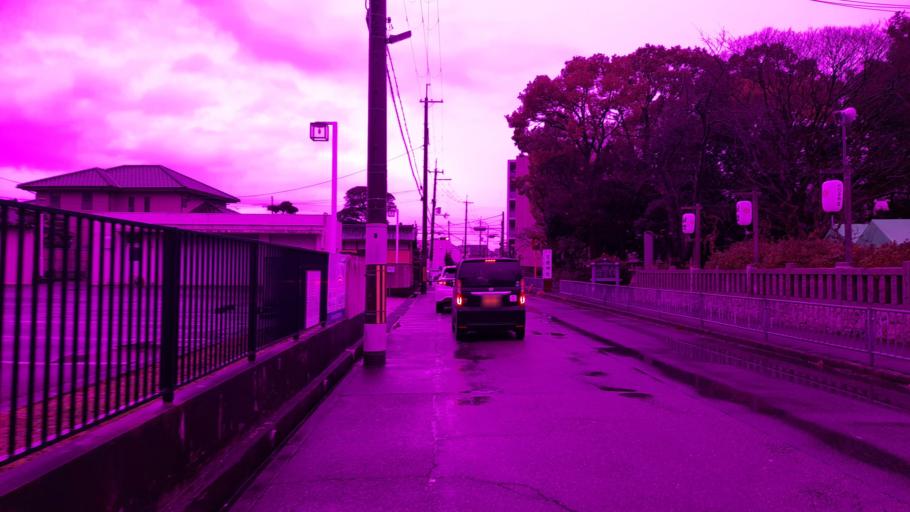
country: JP
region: Osaka
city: Toyonaka
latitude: 34.7575
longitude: 135.4525
